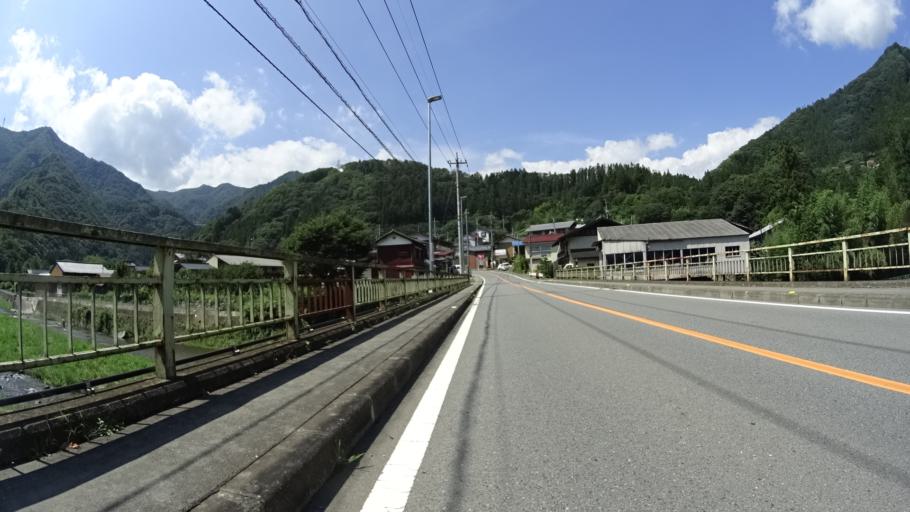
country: JP
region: Gunma
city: Tomioka
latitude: 36.0840
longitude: 138.7853
